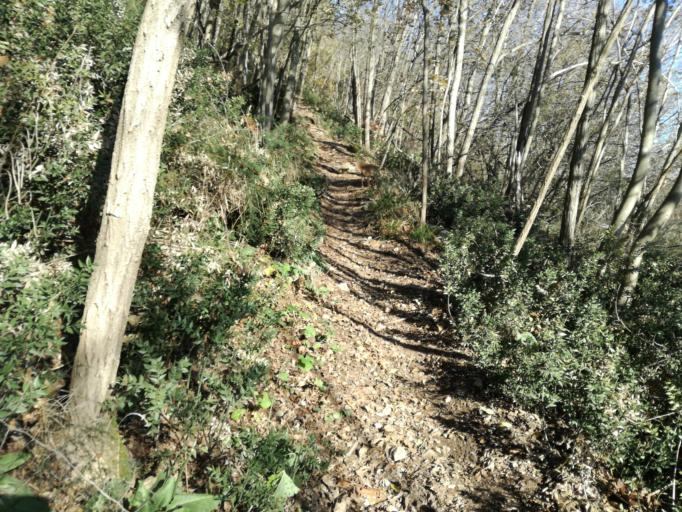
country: IT
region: Veneto
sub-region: Provincia di Padova
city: Arqua Petrarca
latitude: 45.2762
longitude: 11.7293
